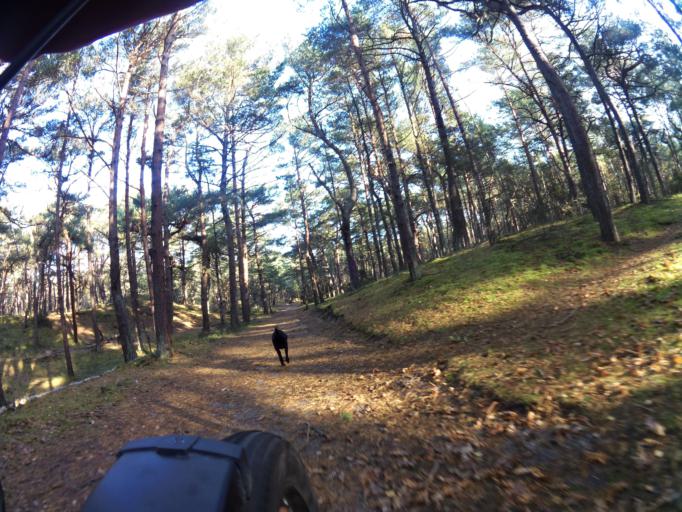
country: PL
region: Pomeranian Voivodeship
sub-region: Powiat pucki
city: Hel
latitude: 54.5977
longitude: 18.8132
